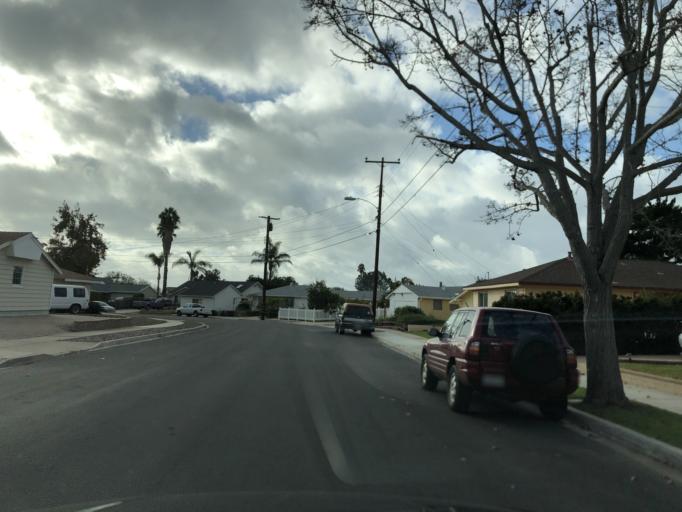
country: US
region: California
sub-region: San Diego County
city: La Jolla
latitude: 32.8174
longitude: -117.1913
